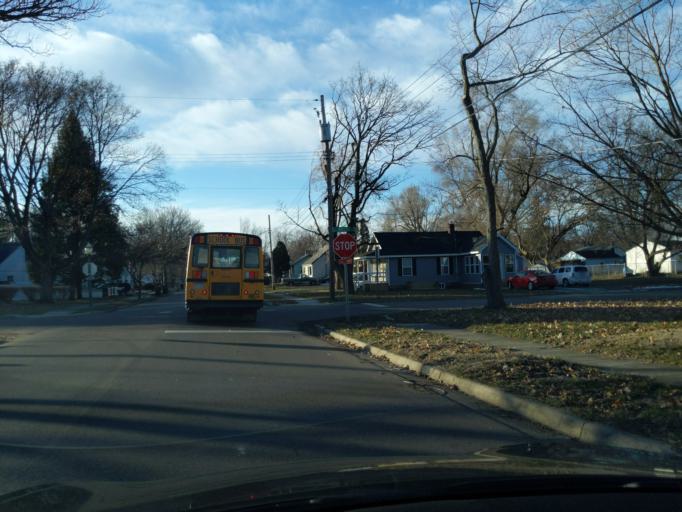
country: US
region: Michigan
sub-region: Ingham County
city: Lansing
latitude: 42.6947
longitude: -84.5619
